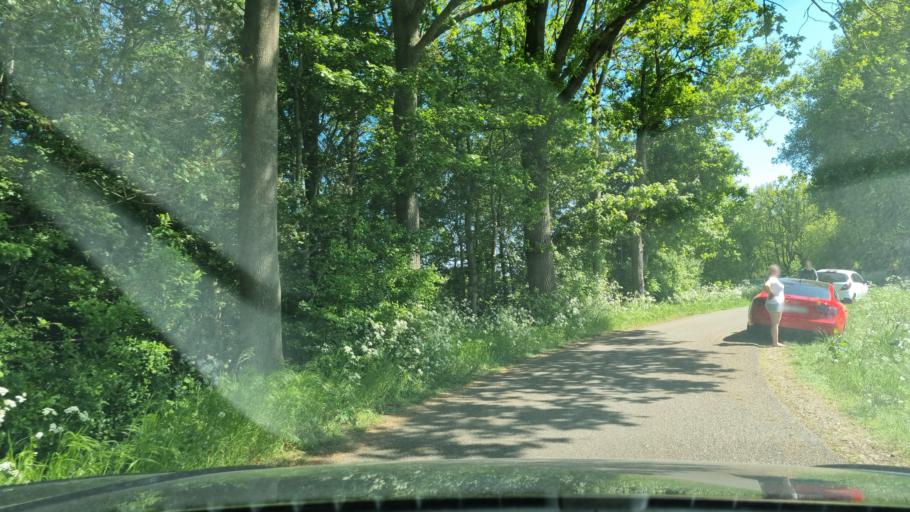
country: NL
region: North Brabant
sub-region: Gemeente Cuijk
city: Cuijk
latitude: 51.7401
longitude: 5.9054
